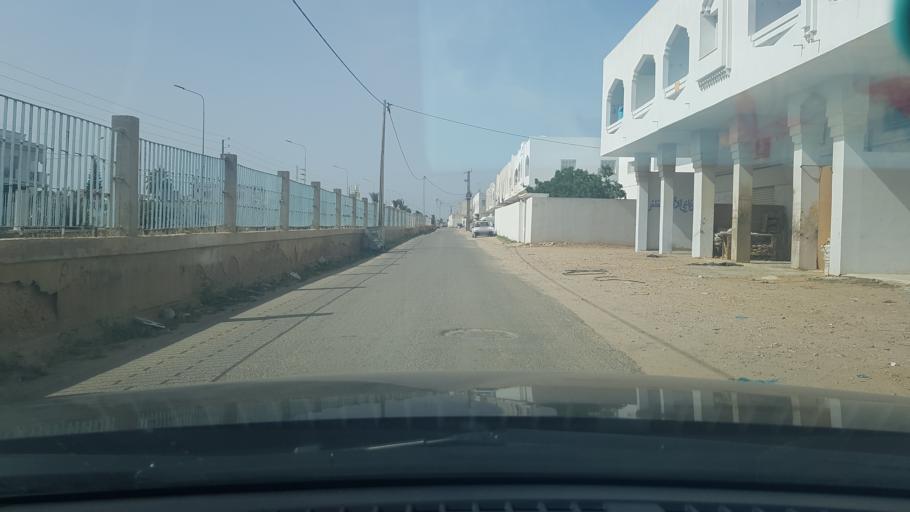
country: TN
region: Safaqis
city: Al Qarmadah
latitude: 34.8111
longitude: 10.7620
